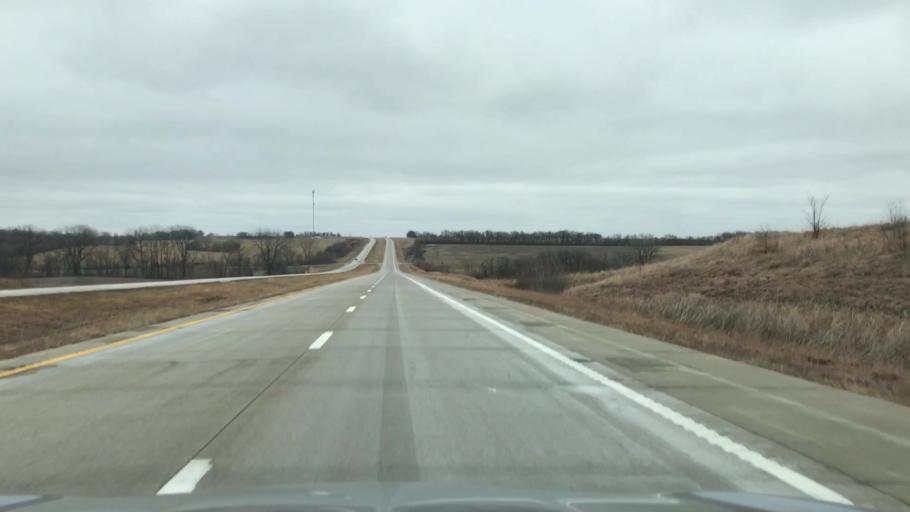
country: US
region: Missouri
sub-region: Caldwell County
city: Hamilton
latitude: 39.7346
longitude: -93.7844
